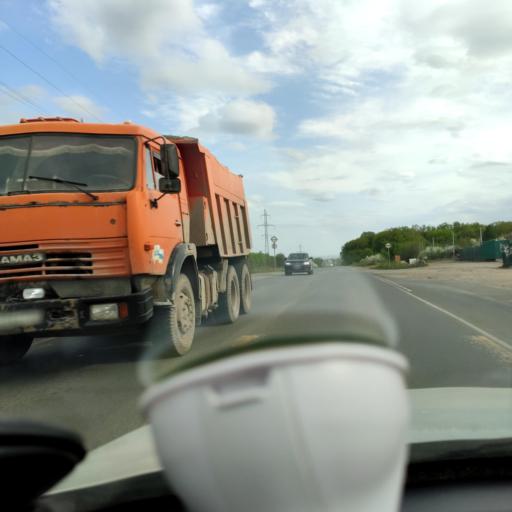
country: RU
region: Samara
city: Novosemeykino
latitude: 53.3325
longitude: 50.2555
